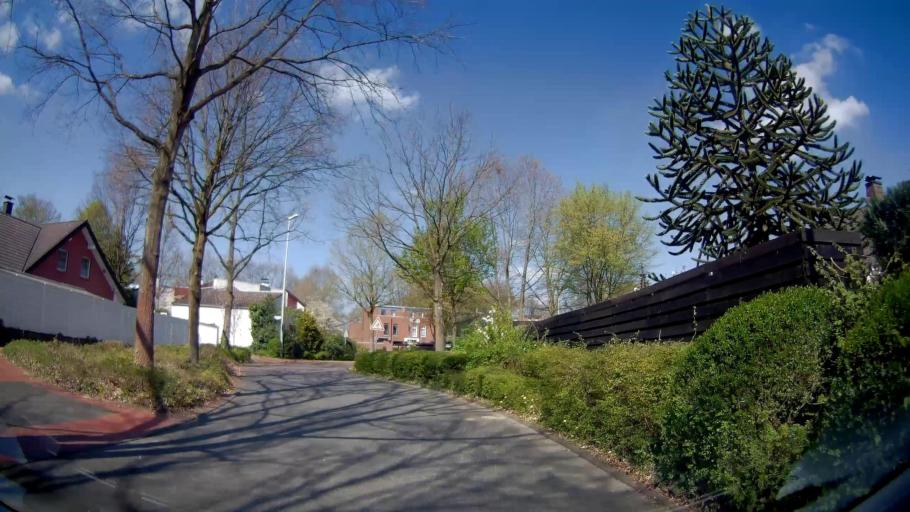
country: DE
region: North Rhine-Westphalia
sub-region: Regierungsbezirk Munster
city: Klein Reken
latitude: 51.7347
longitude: 7.0445
